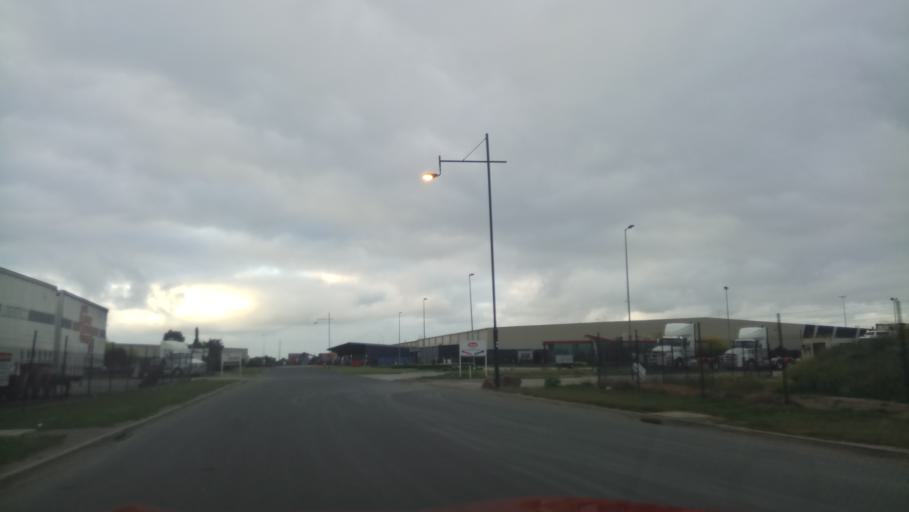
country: AU
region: Victoria
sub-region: Hobsons Bay
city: Laverton
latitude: -37.8549
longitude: 144.7889
